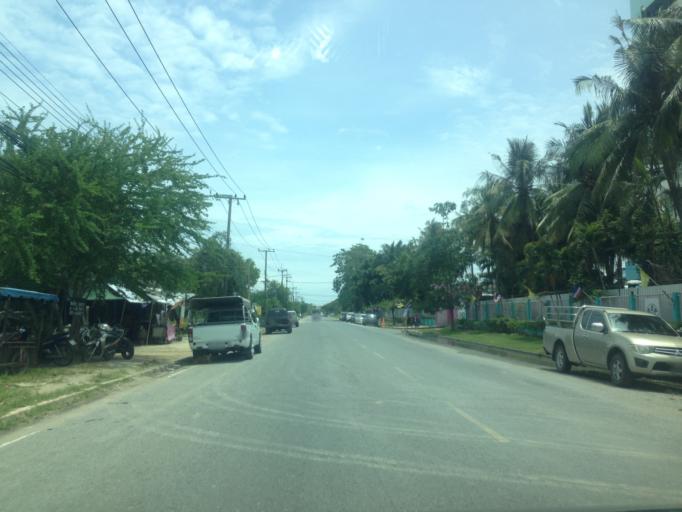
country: TH
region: Chon Buri
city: Chon Buri
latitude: 13.3445
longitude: 100.9540
